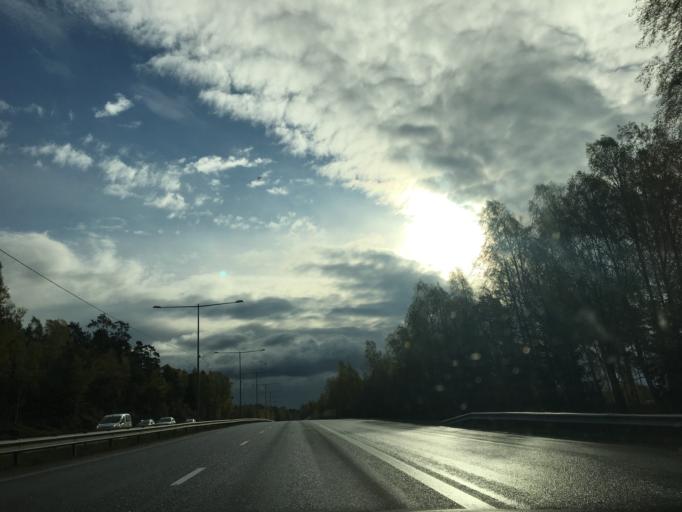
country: SE
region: Vaermland
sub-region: Karlstads Kommun
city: Karlstad
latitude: 59.3988
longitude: 13.5337
